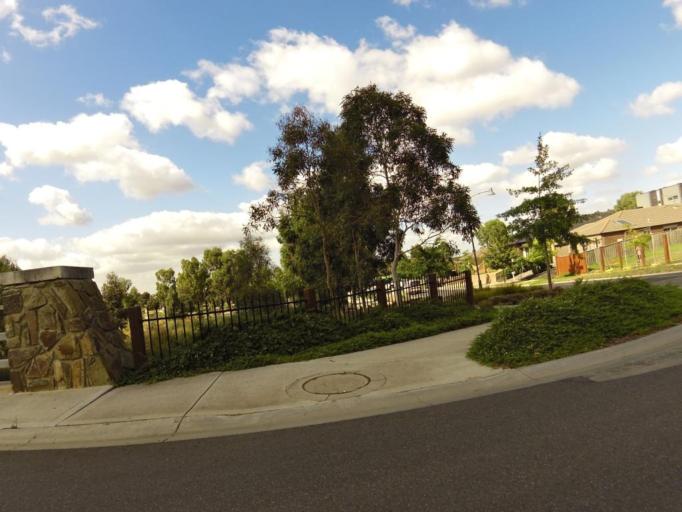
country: AU
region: Victoria
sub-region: Whittlesea
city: Mernda
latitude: -37.6194
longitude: 145.0694
